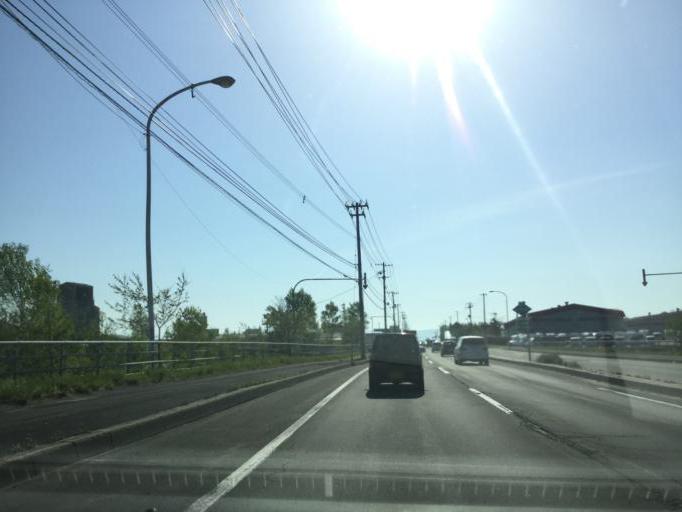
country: JP
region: Hokkaido
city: Kitahiroshima
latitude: 42.9993
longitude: 141.5469
